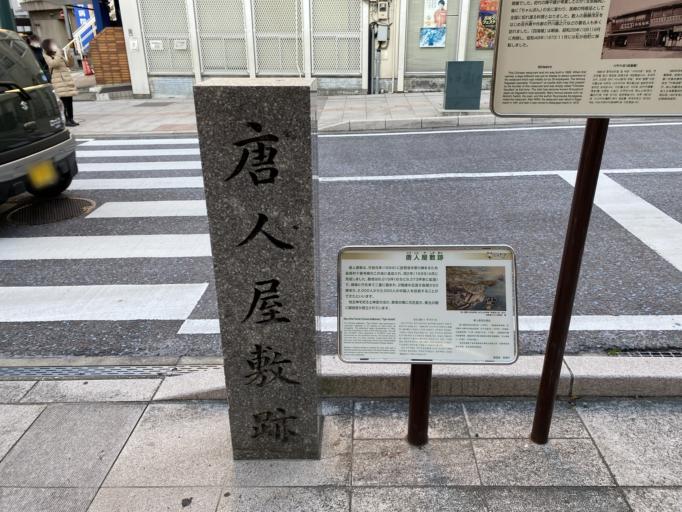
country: JP
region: Nagasaki
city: Nagasaki-shi
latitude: 32.7399
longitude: 129.8763
